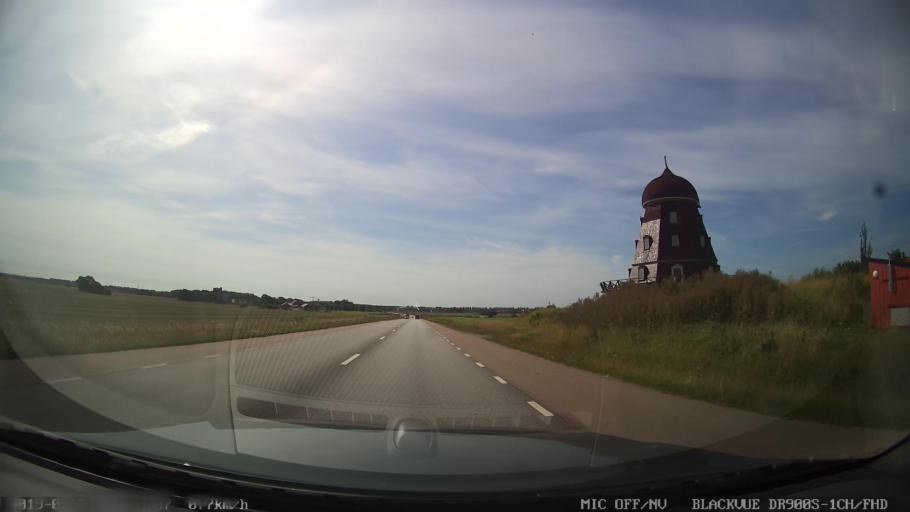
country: SE
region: Skane
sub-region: Helsingborg
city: Glumslov
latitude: 55.9136
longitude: 12.8245
